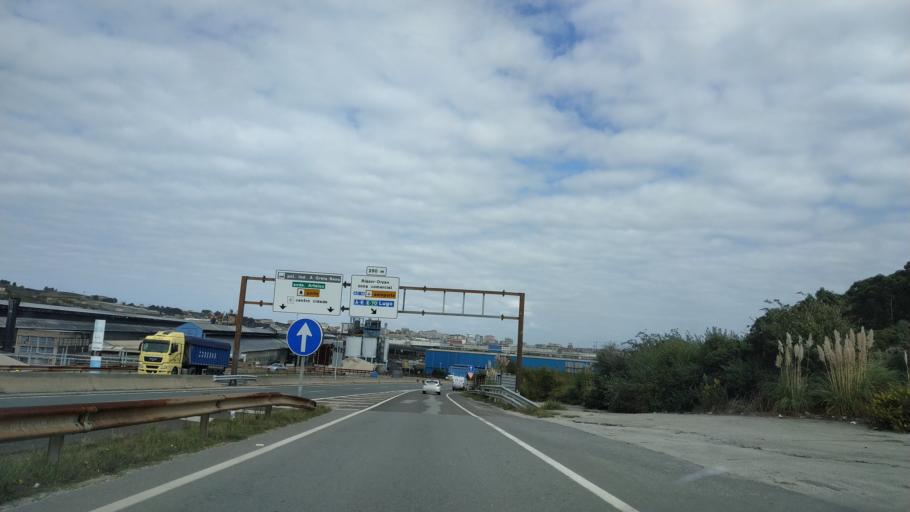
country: ES
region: Galicia
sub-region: Provincia da Coruna
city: A Coruna
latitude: 43.3431
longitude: -8.4415
